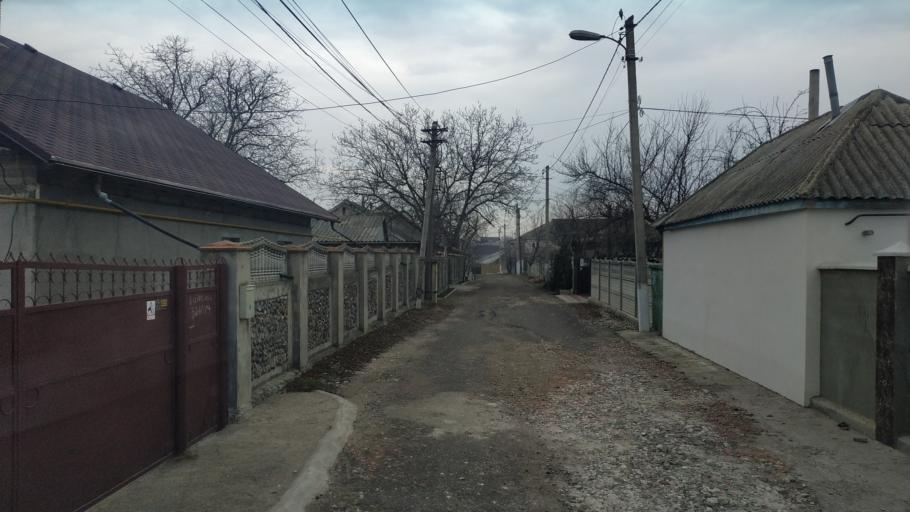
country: MD
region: Chisinau
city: Singera
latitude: 46.9187
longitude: 28.9634
